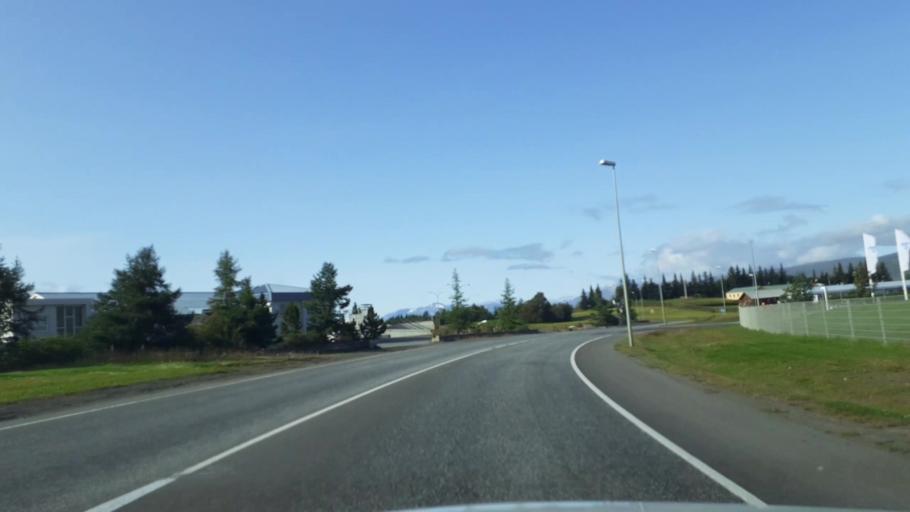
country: IS
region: Northeast
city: Akureyri
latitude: 65.6760
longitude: -18.1294
